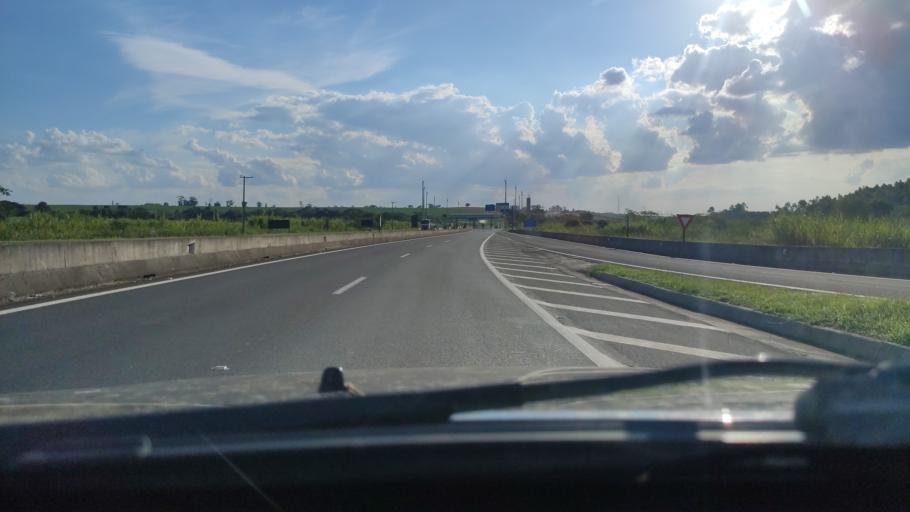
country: BR
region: Sao Paulo
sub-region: Mogi-Mirim
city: Mogi Mirim
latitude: -22.4564
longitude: -46.8983
